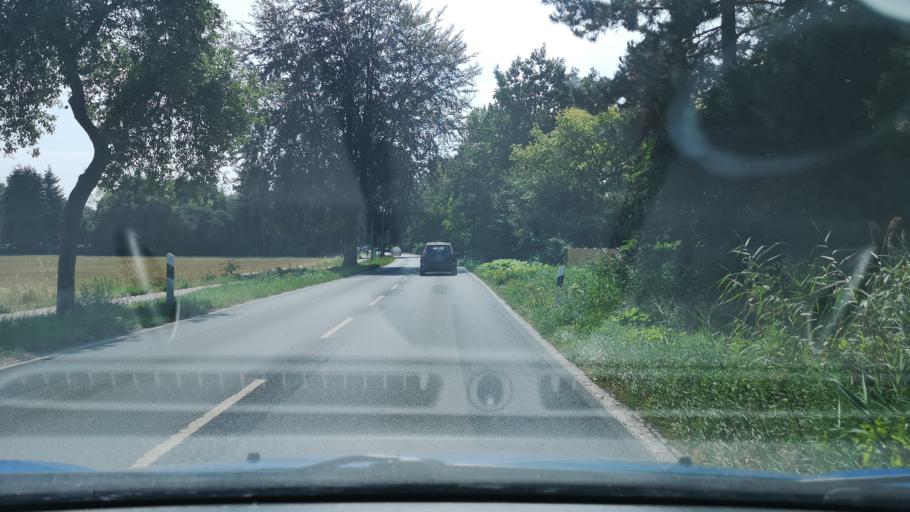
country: DE
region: Lower Saxony
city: Isernhagen Farster Bauerschaft
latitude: 52.4402
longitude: 9.8011
